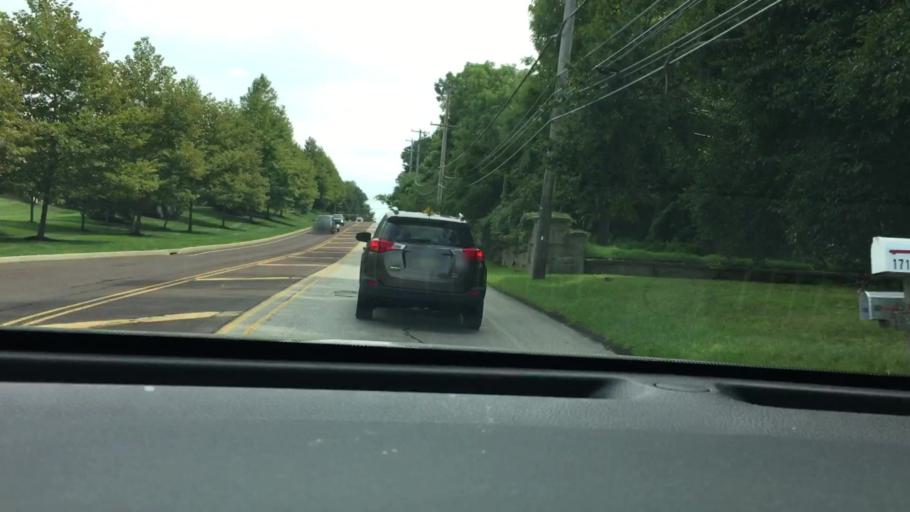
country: US
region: Pennsylvania
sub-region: Montgomery County
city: Bryn Athyn
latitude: 40.1568
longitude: -75.0712
